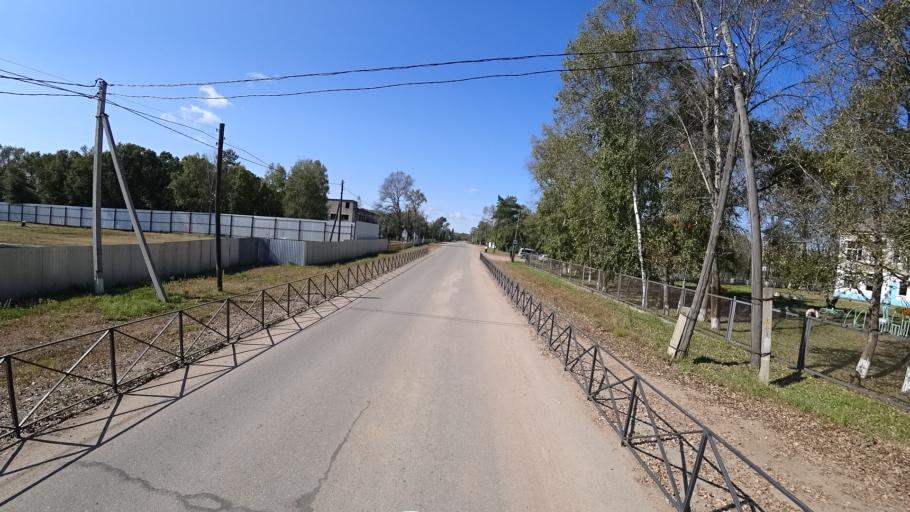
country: RU
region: Amur
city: Arkhara
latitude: 49.4029
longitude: 130.1403
